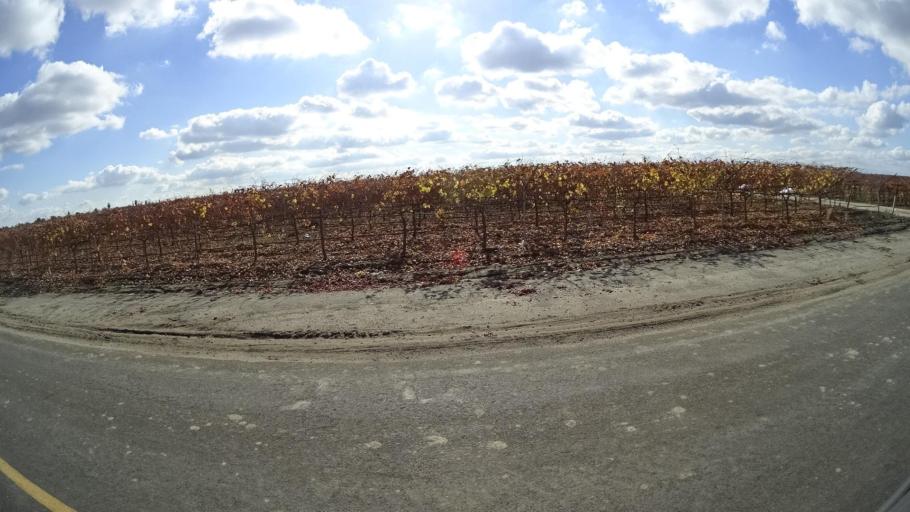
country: US
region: California
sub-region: Kern County
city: McFarland
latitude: 35.6816
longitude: -119.2450
